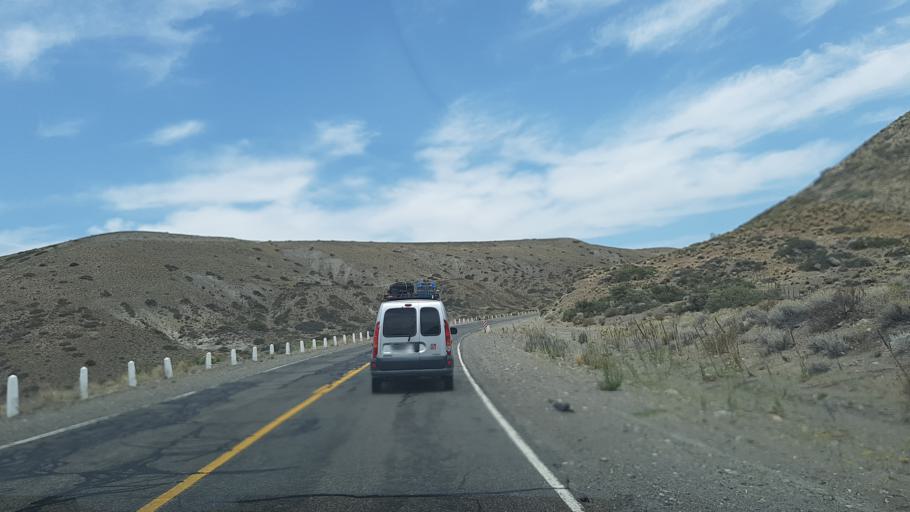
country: AR
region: Rio Negro
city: Pilcaniyeu
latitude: -40.4691
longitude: -70.6570
